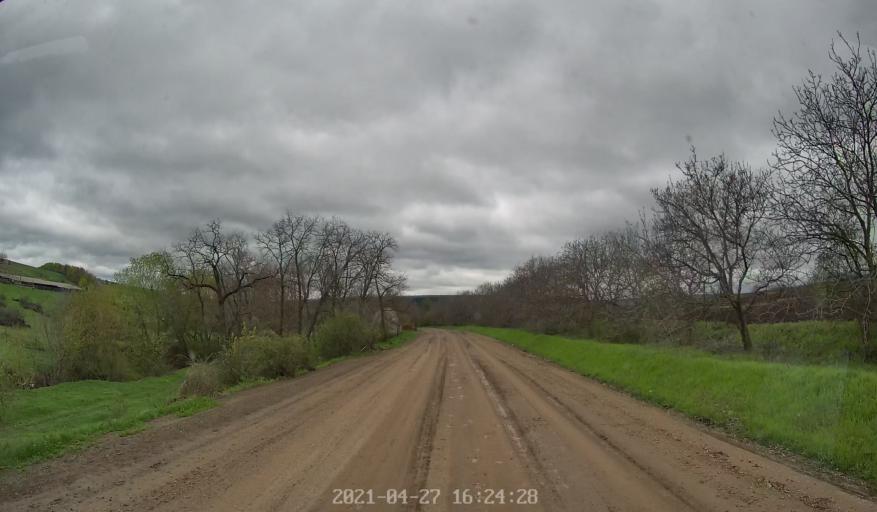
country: MD
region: Chisinau
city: Singera
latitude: 46.9916
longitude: 29.0208
